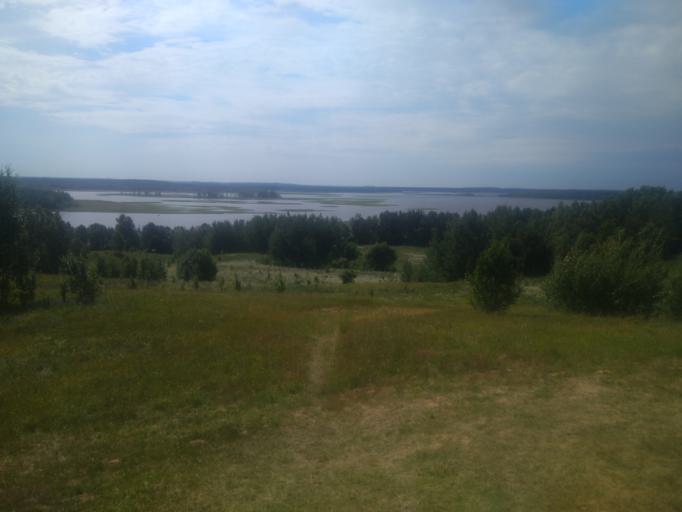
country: BY
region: Vitebsk
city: Braslaw
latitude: 55.7199
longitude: 27.0557
